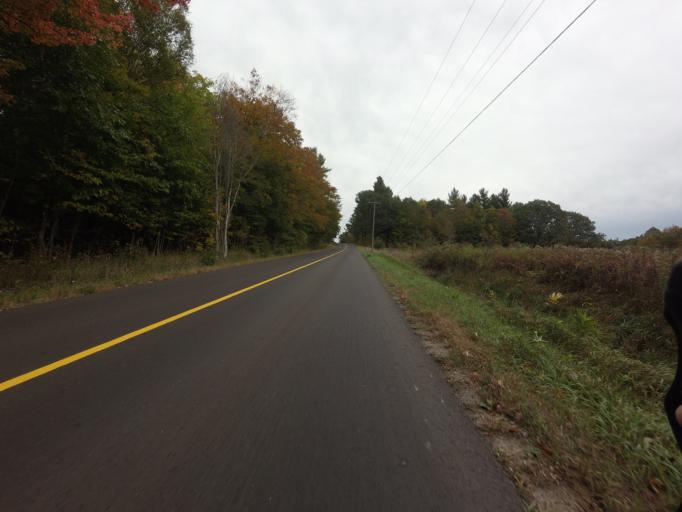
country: CA
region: Ontario
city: Gananoque
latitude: 44.5743
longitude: -76.0977
